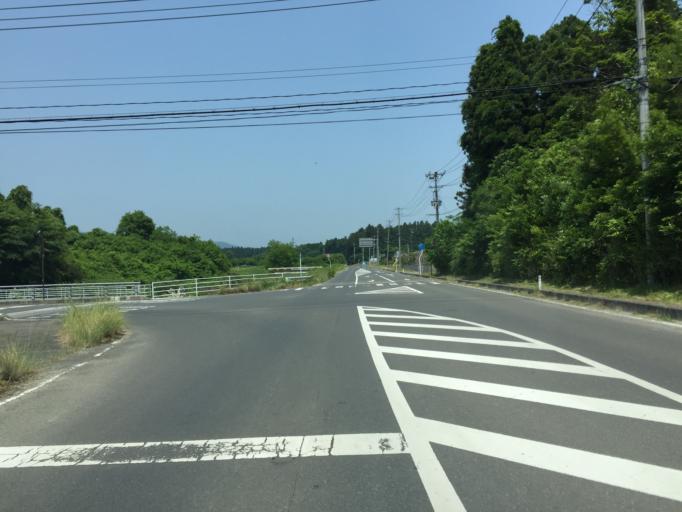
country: JP
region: Miyagi
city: Marumori
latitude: 37.8359
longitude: 140.8941
